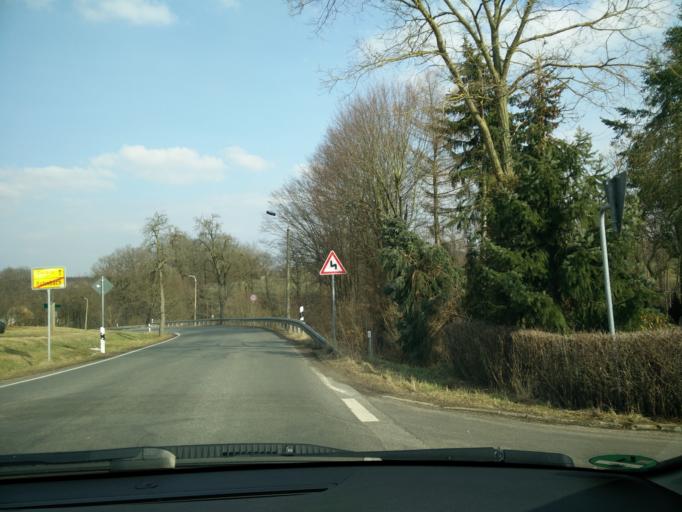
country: DE
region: Saxony
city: Colditz
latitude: 51.1211
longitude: 12.7921
